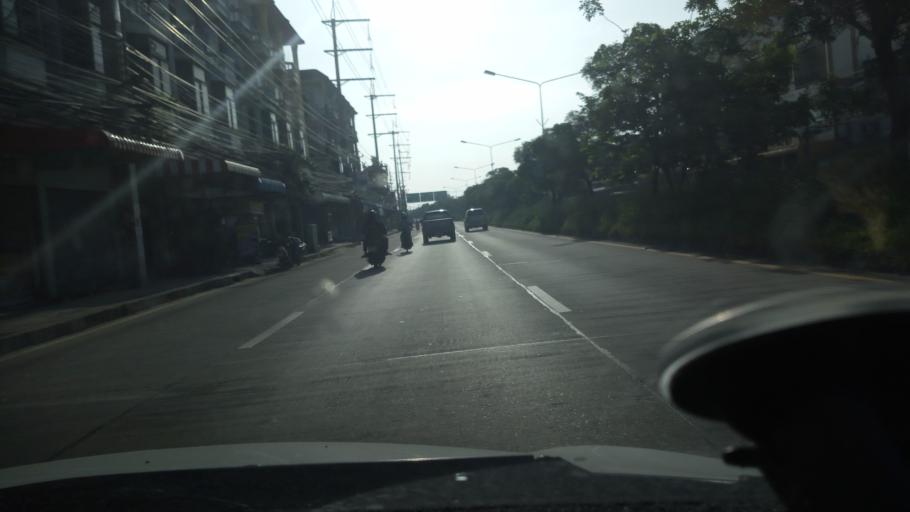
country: TH
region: Chon Buri
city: Phan Thong
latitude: 13.4231
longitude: 101.1055
